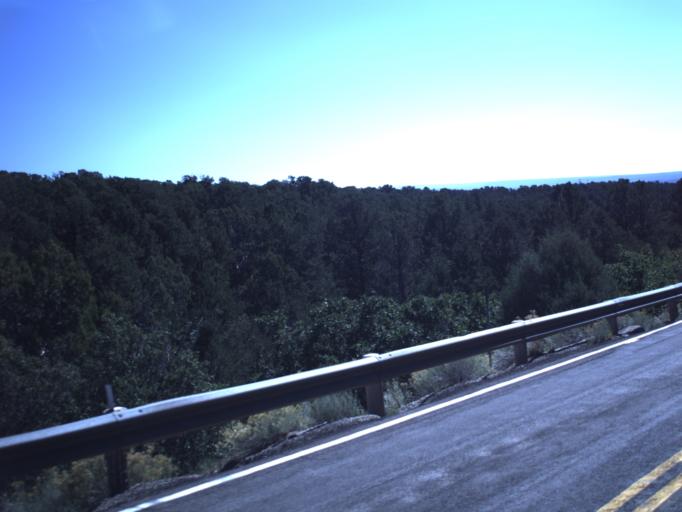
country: US
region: Utah
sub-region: Grand County
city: Moab
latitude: 38.3245
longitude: -109.2258
